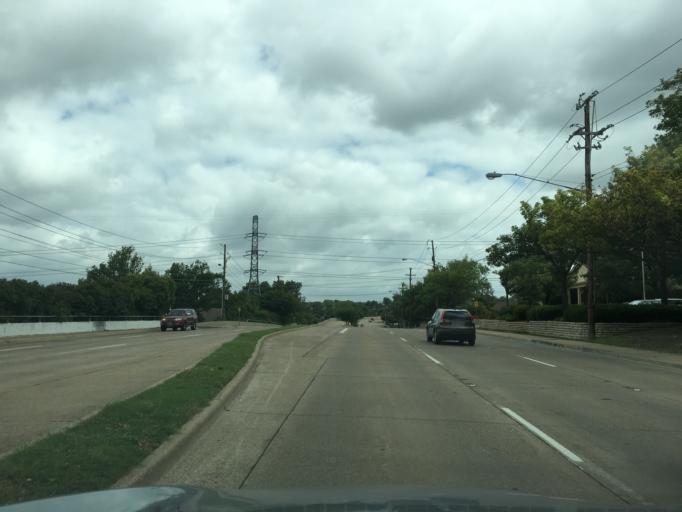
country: US
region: Texas
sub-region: Dallas County
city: Richardson
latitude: 32.8875
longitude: -96.7416
